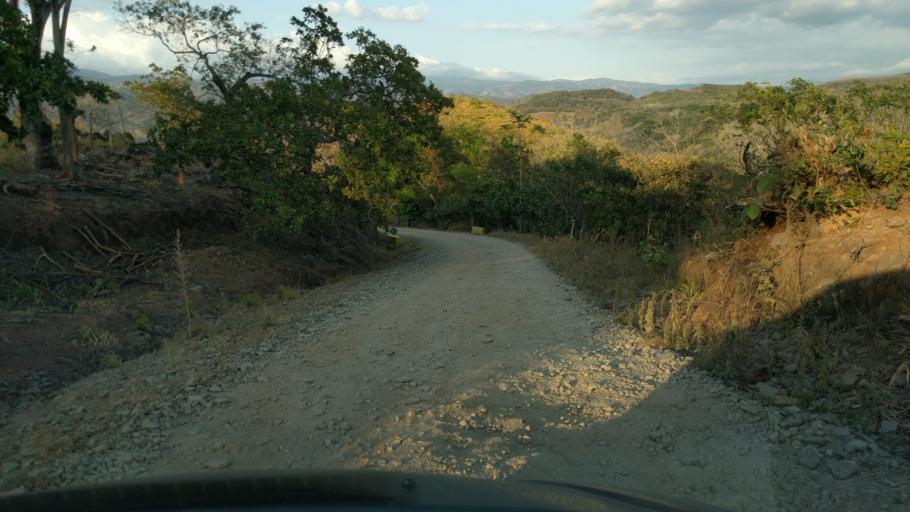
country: CR
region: Puntarenas
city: Esparza
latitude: 10.0273
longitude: -84.6987
